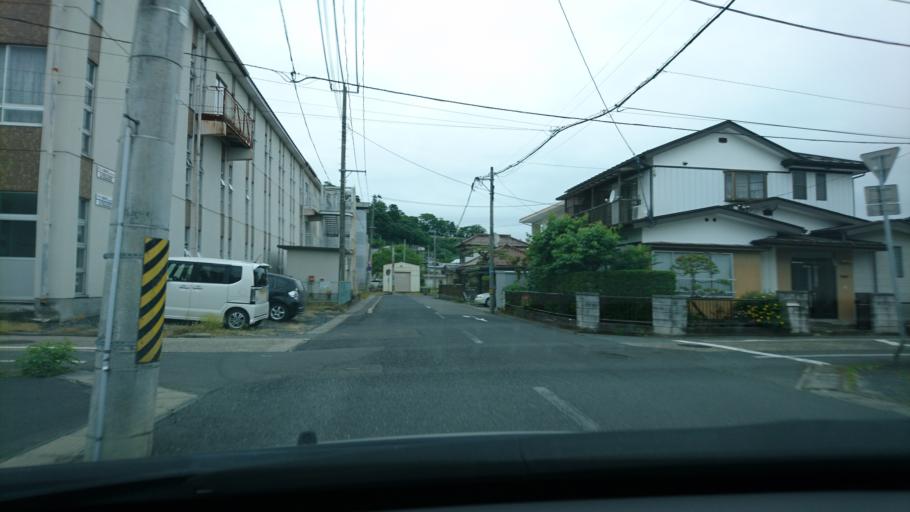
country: JP
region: Iwate
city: Ichinoseki
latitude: 38.9240
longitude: 141.1336
